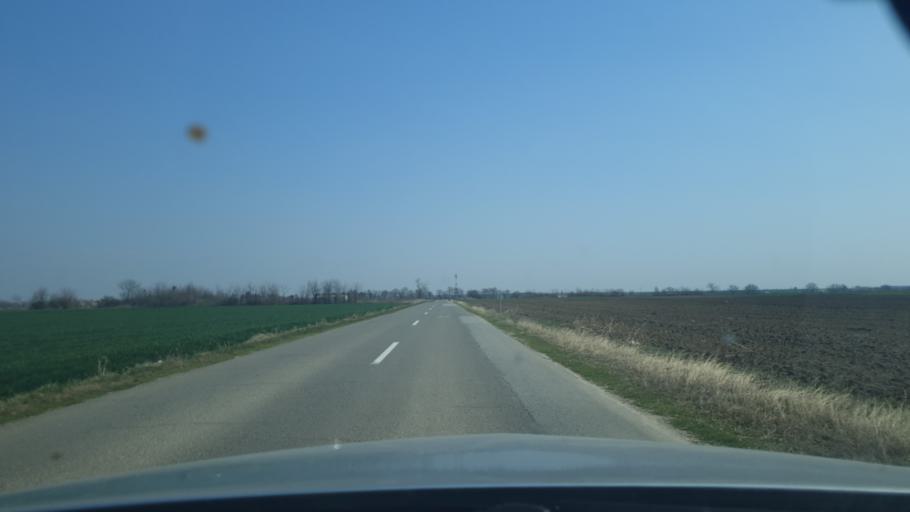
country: RS
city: Sasinci
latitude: 45.0477
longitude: 19.7119
